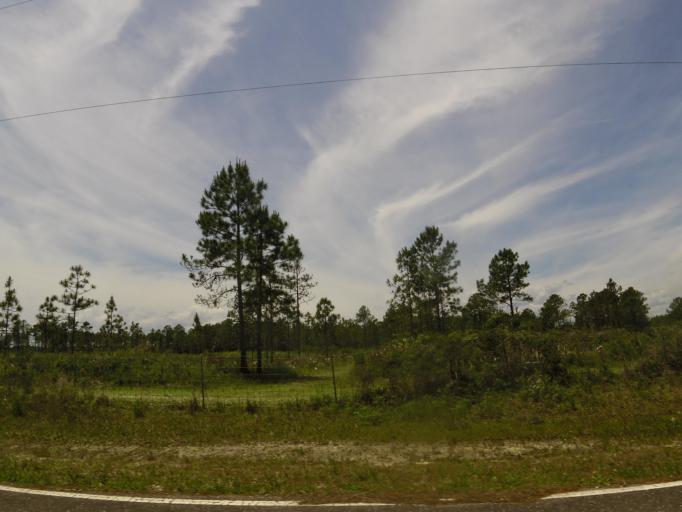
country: US
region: Florida
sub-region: Duval County
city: Atlantic Beach
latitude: 30.4785
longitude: -81.4872
